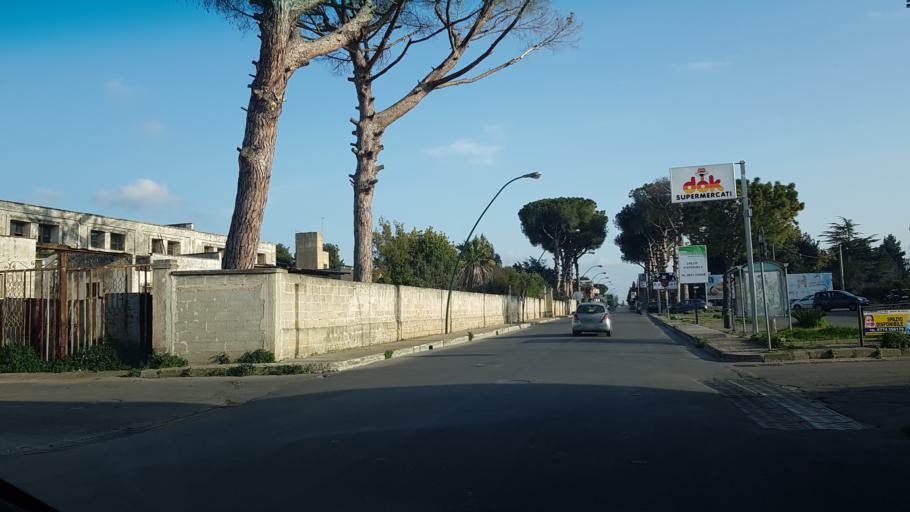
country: IT
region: Apulia
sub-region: Provincia di Lecce
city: Squinzano
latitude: 40.4328
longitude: 18.0489
